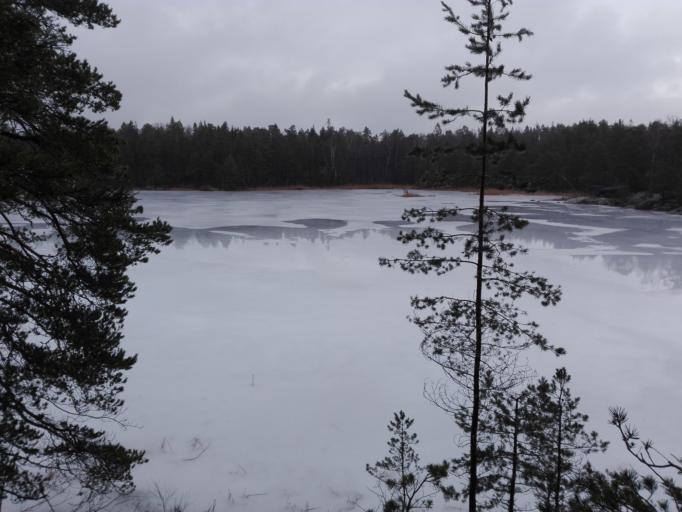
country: SE
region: Stockholm
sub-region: Nacka Kommun
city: Fisksatra
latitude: 59.2763
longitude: 18.2556
